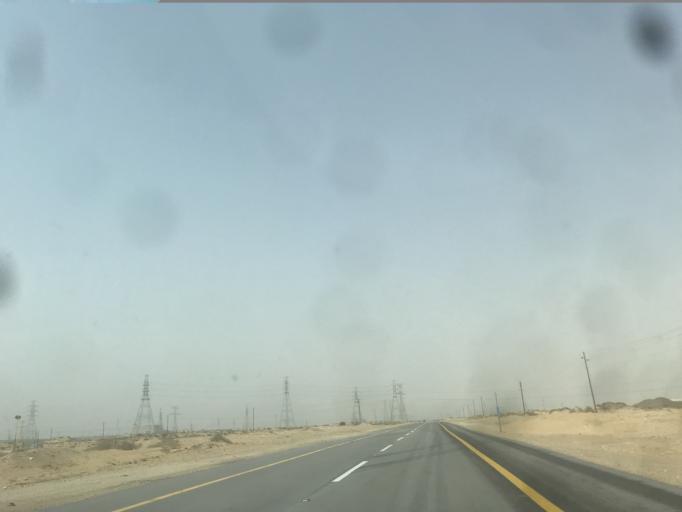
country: SA
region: Eastern Province
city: Abqaiq
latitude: 25.9365
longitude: 49.7251
